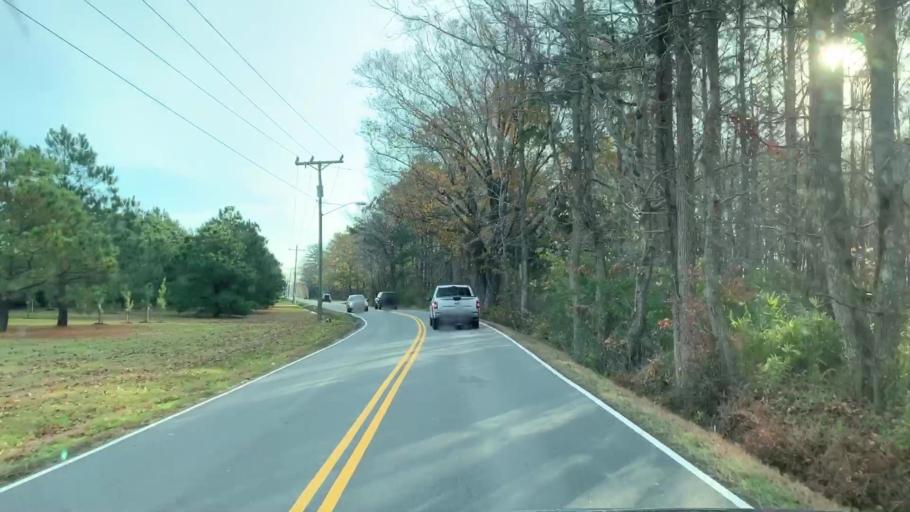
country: US
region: Virginia
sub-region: City of Virginia Beach
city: Virginia Beach
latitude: 36.7236
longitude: -76.0658
